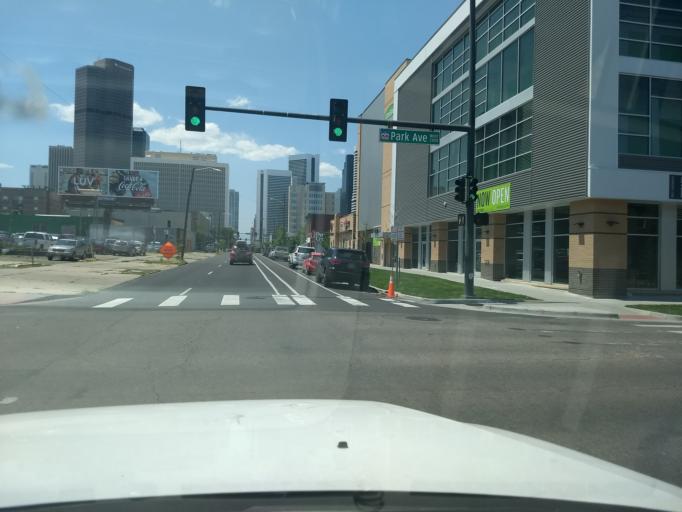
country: US
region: Colorado
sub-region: Denver County
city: Denver
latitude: 39.7531
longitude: -104.9854
